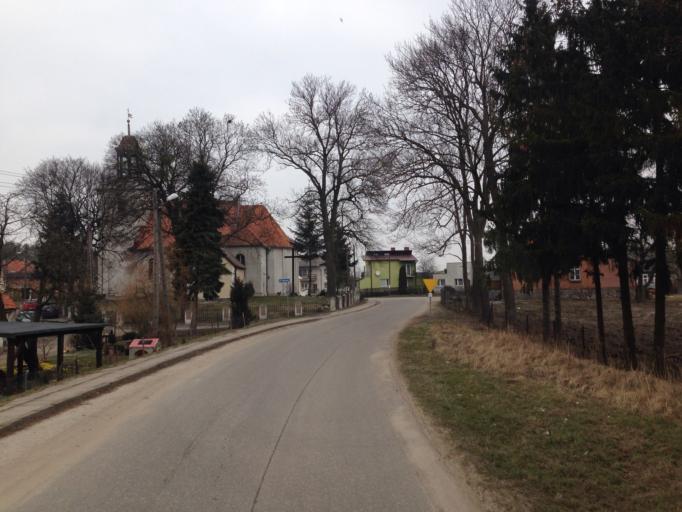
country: PL
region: Pomeranian Voivodeship
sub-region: Powiat kwidzynski
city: Sadlinki
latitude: 53.7413
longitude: 18.8240
